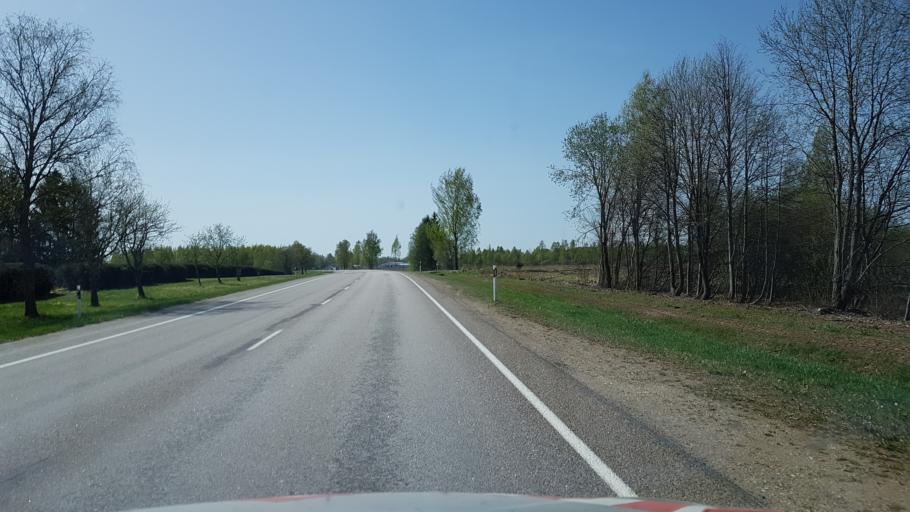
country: EE
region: Valgamaa
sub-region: Valga linn
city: Valga
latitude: 57.8008
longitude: 26.0358
